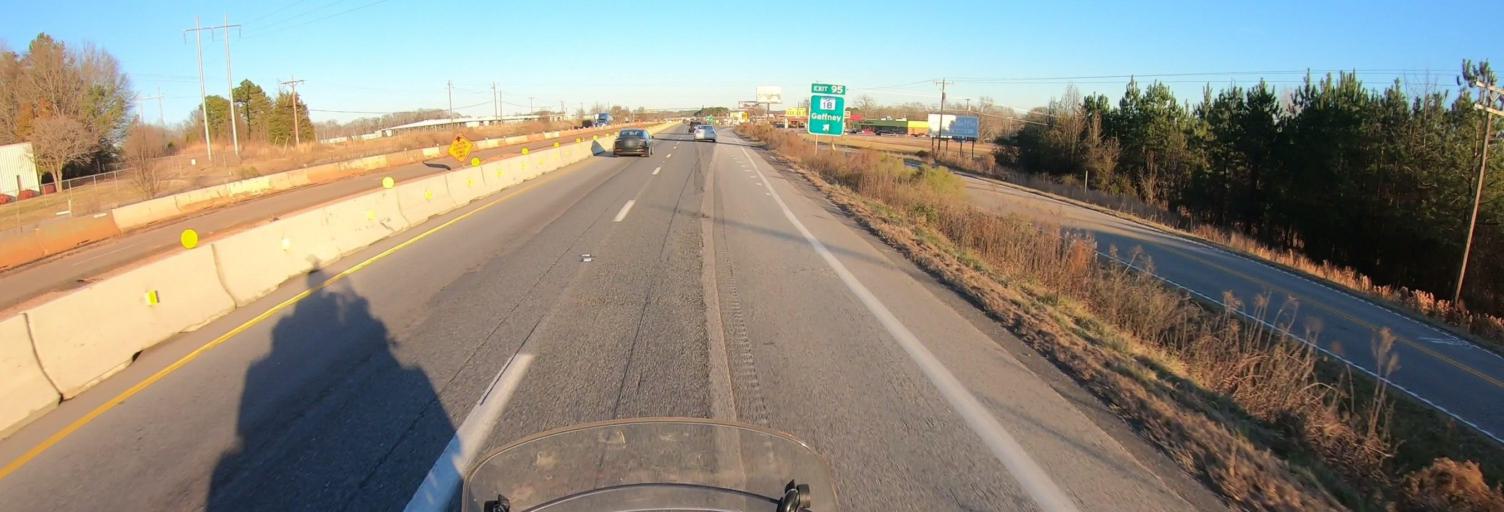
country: US
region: South Carolina
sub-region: Cherokee County
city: East Gaffney
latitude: 35.1014
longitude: -81.6372
